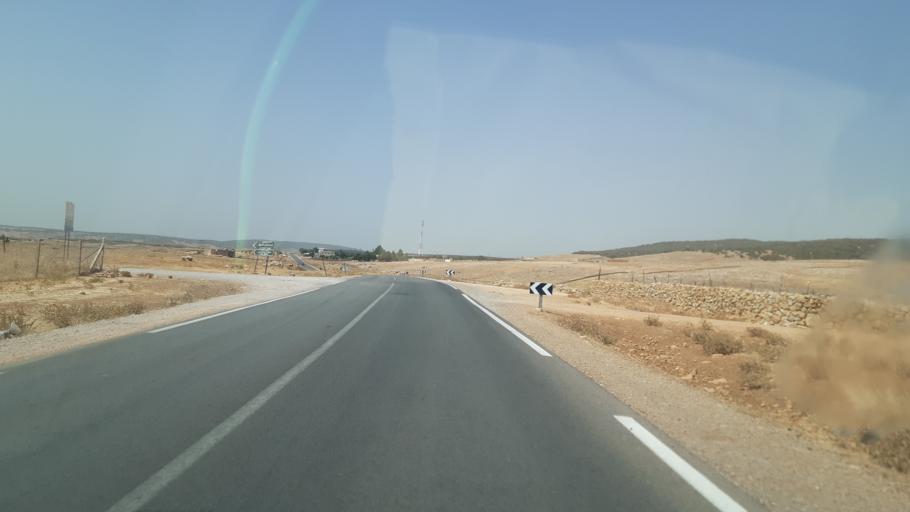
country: MA
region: Meknes-Tafilalet
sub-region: Ifrane
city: Ifrane
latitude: 33.6098
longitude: -5.0813
